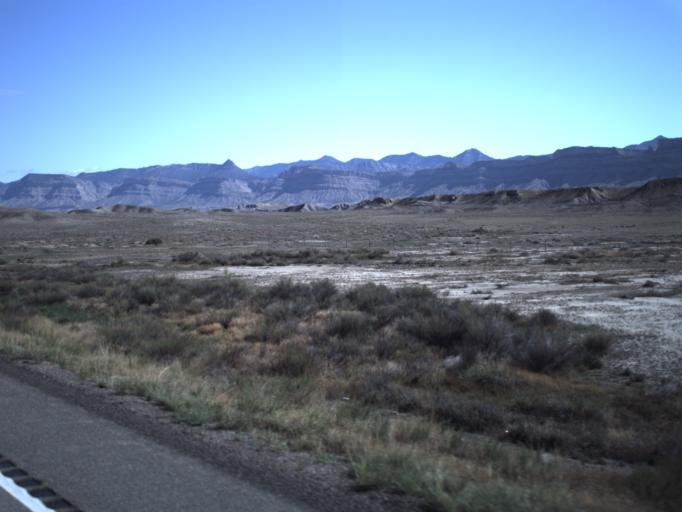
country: US
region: Utah
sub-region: Carbon County
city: East Carbon City
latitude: 39.3100
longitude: -110.3606
